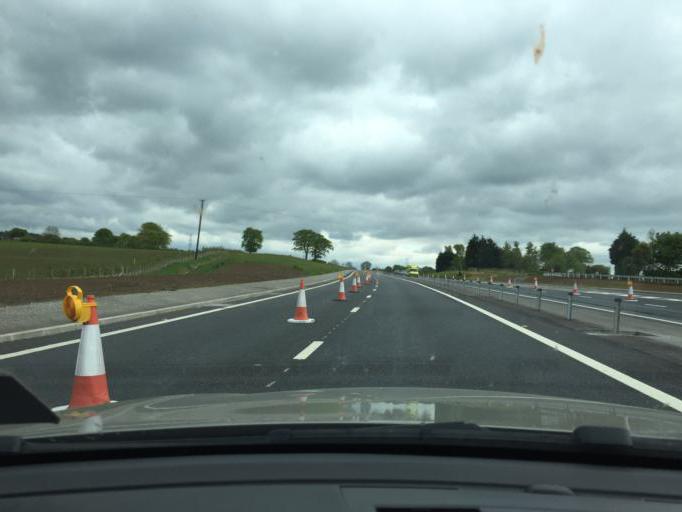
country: GB
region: Northern Ireland
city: Carnmoney
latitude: 54.7385
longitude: -5.9626
